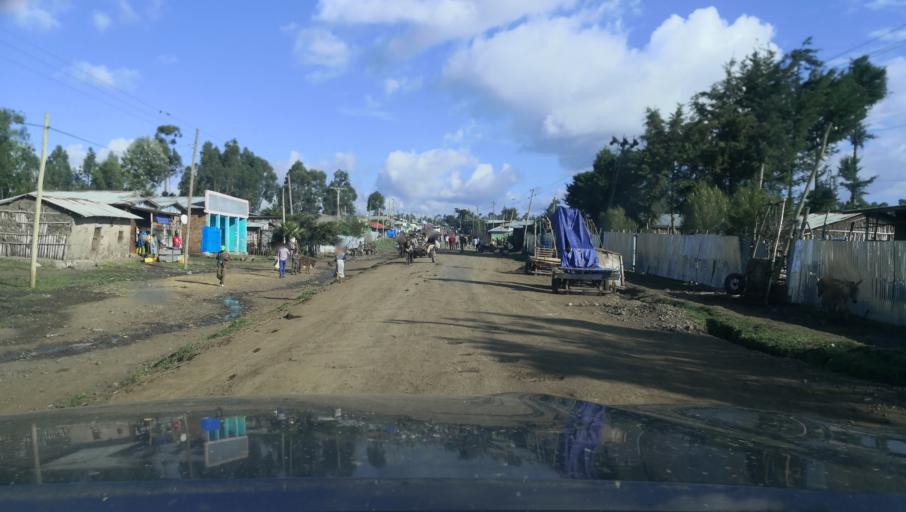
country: ET
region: Oromiya
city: Tulu Bolo
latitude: 8.4705
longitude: 38.2499
